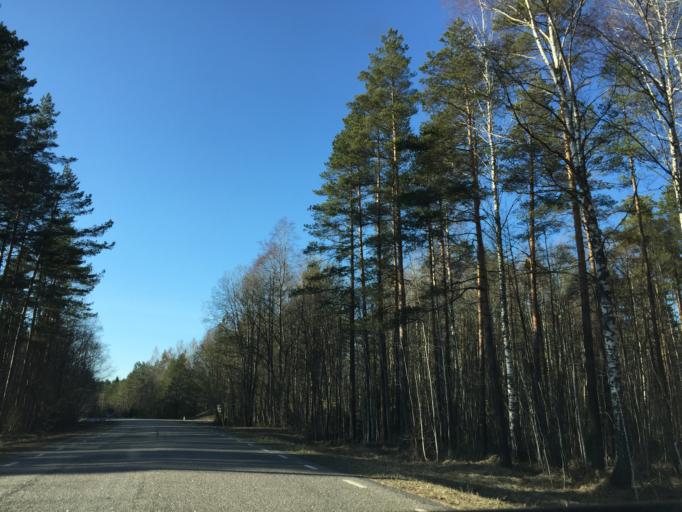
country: EE
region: Ida-Virumaa
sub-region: Sillamaee linn
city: Sillamae
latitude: 59.0758
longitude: 27.6942
